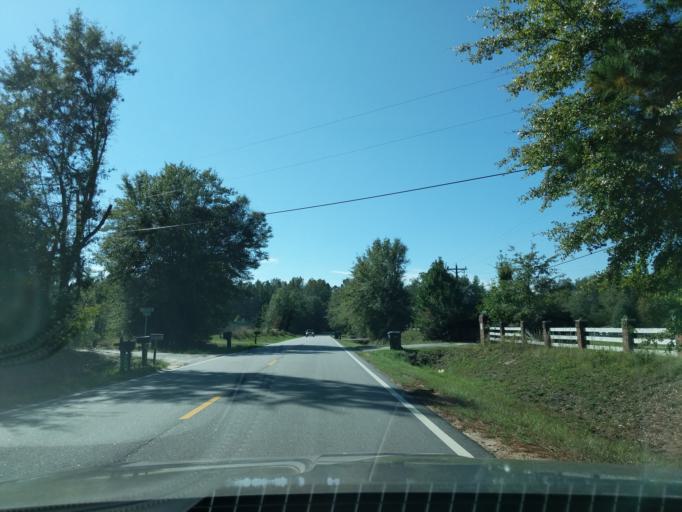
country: US
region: Georgia
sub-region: Richmond County
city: Hephzibah
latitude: 33.3041
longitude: -82.0188
